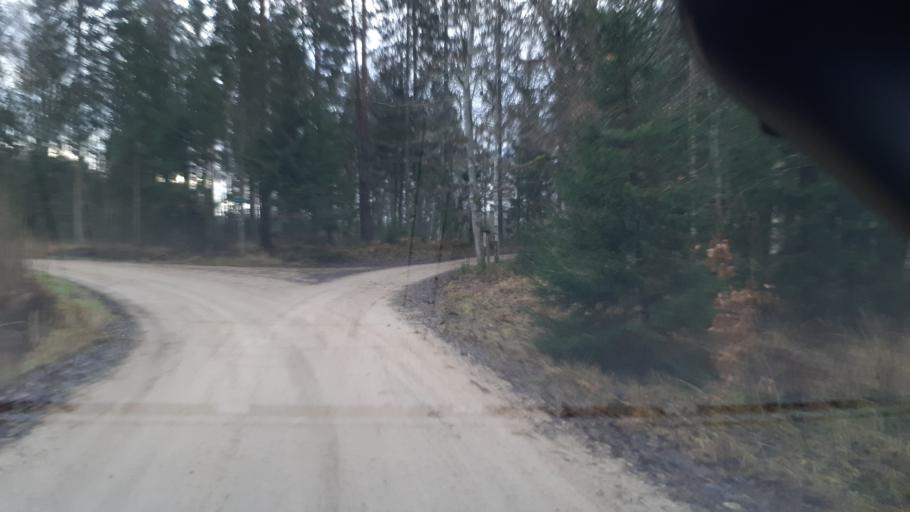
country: LV
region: Kuldigas Rajons
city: Kuldiga
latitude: 56.9019
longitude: 21.9090
